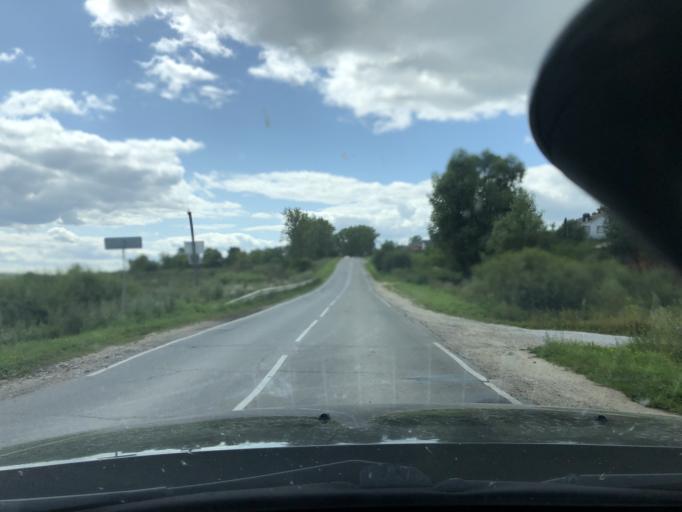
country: RU
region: Tula
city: Revyakino
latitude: 54.3608
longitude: 37.6400
